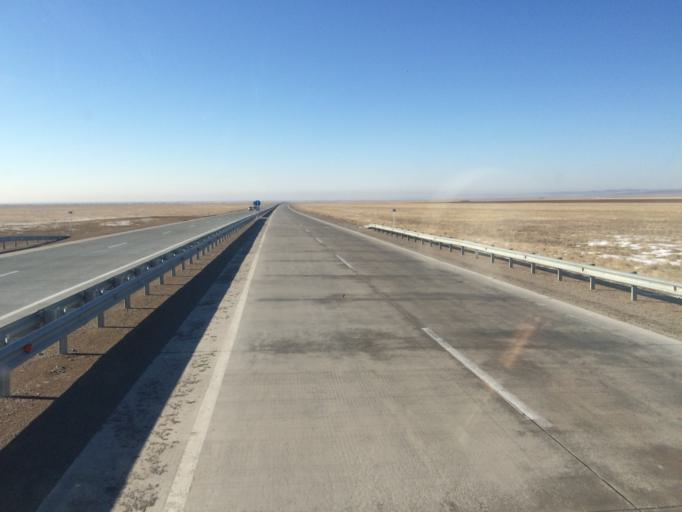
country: KZ
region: Zhambyl
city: Georgiyevka
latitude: 43.3426
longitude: 74.4025
